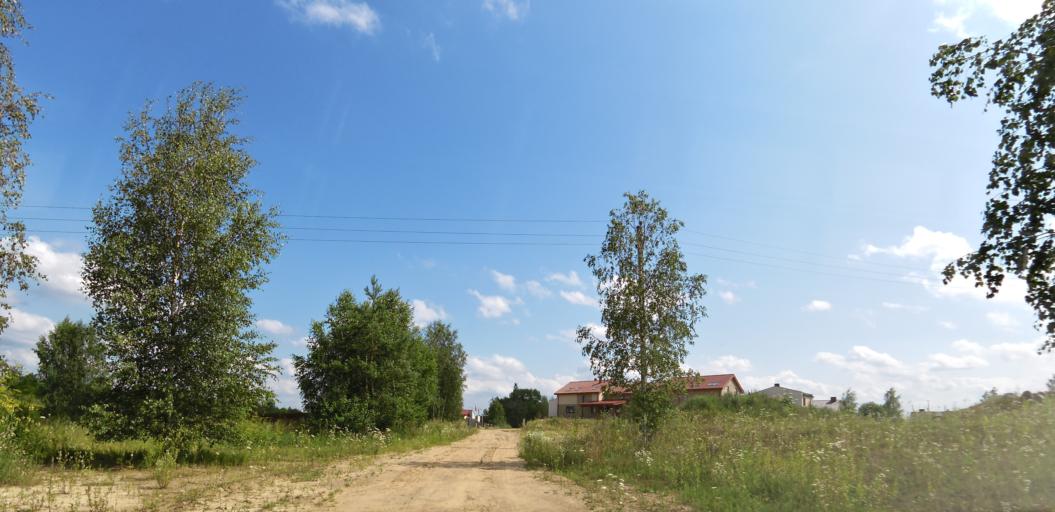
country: LT
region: Vilnius County
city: Pilaite
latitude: 54.7163
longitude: 25.1640
